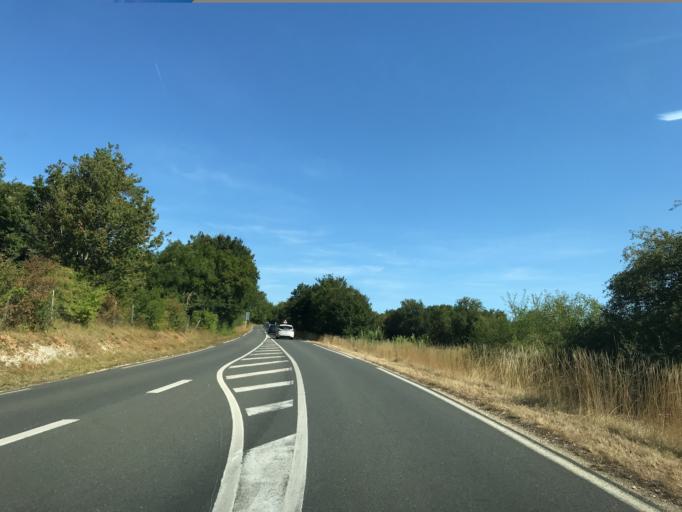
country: FR
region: Limousin
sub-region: Departement de la Correze
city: Larche
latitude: 45.0529
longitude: 1.3810
